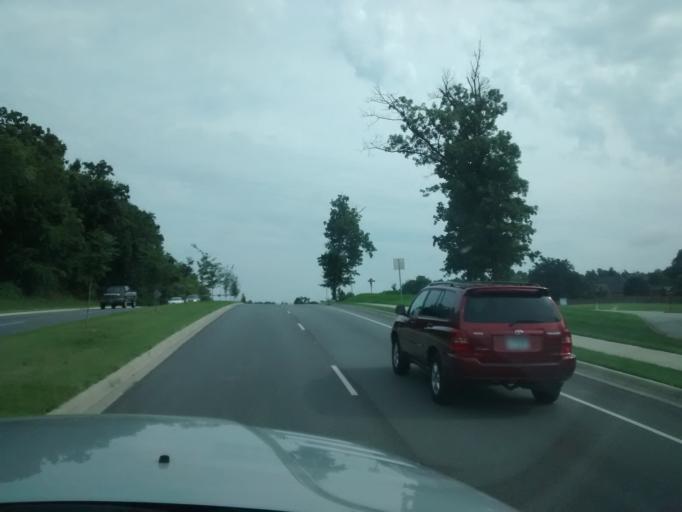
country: US
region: Arkansas
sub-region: Washington County
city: Johnson
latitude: 36.1375
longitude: -94.1177
